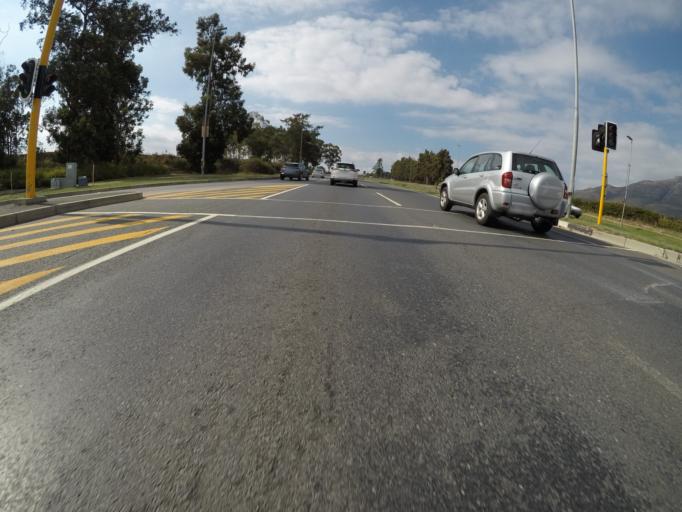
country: ZA
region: Western Cape
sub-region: Cape Winelands District Municipality
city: Stellenbosch
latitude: -33.9691
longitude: 18.8442
